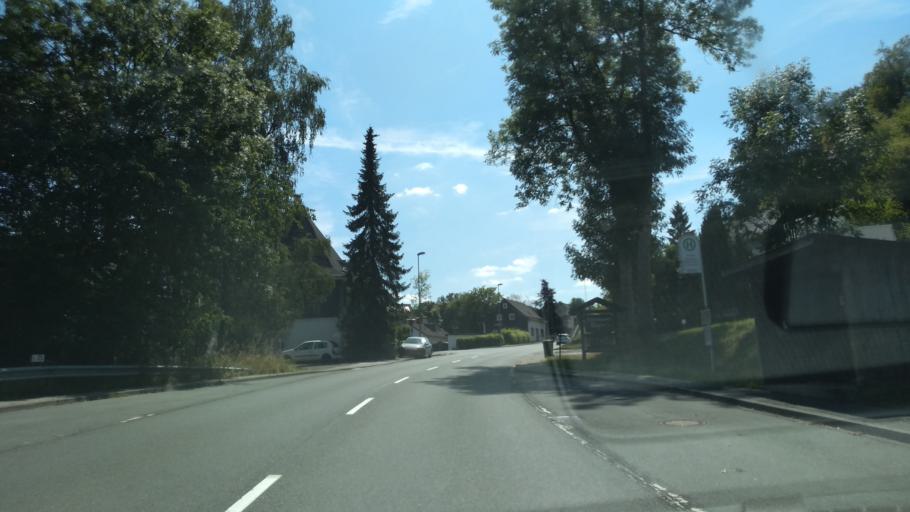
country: DE
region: North Rhine-Westphalia
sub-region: Regierungsbezirk Arnsberg
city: Olpe
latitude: 51.0530
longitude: 7.8584
